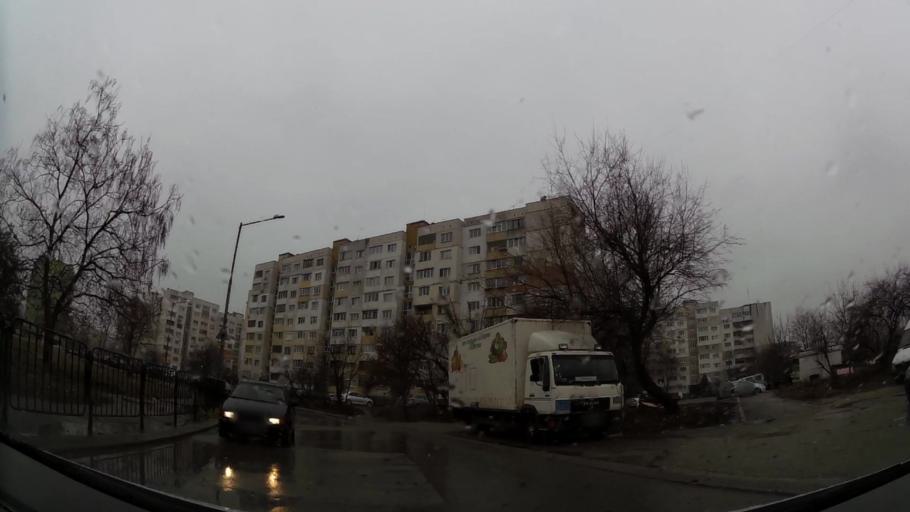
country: BG
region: Sofia-Capital
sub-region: Stolichna Obshtina
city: Sofia
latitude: 42.6457
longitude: 23.4093
